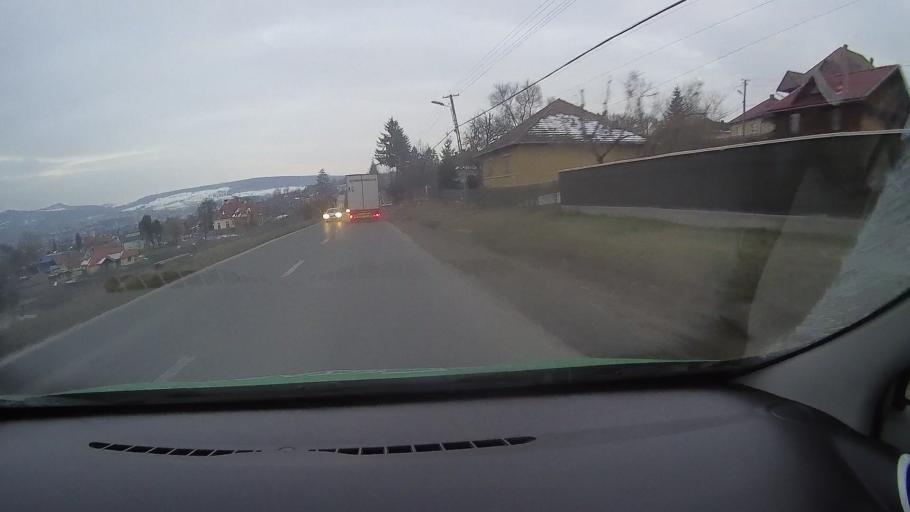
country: RO
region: Harghita
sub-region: Municipiul Odorheiu Secuiesc
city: Odorheiu Secuiesc
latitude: 46.3184
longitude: 25.2803
